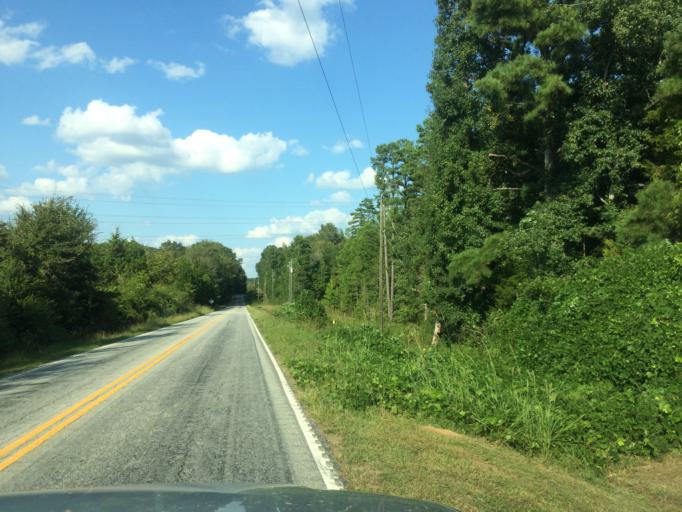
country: US
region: South Carolina
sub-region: Greenville County
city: Fountain Inn
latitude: 34.5568
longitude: -82.2123
